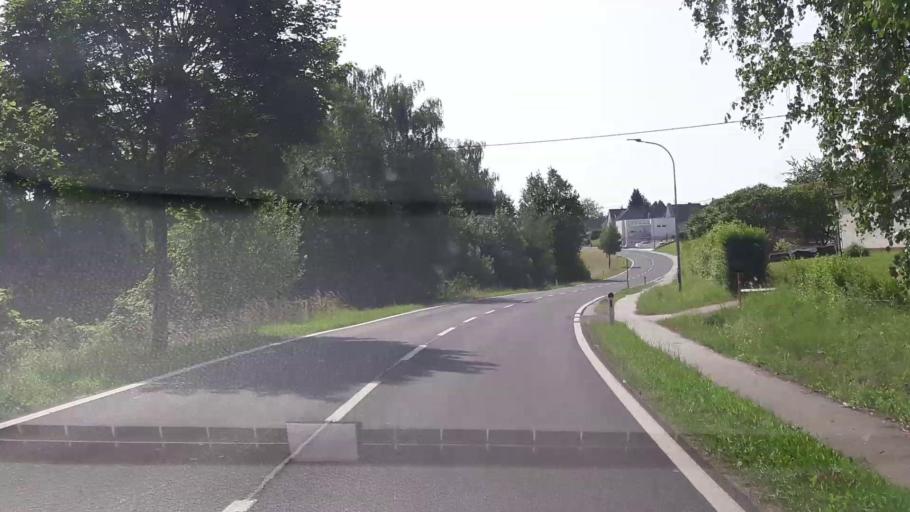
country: AT
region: Burgenland
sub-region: Politischer Bezirk Gussing
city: Stegersbach
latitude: 47.1618
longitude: 16.1395
